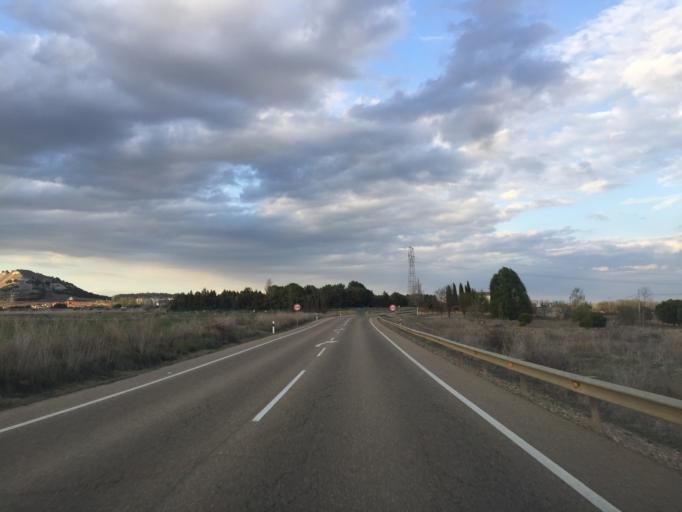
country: ES
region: Castille and Leon
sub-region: Provincia de Palencia
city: Soto de Cerrato
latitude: 41.9704
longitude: -4.4423
